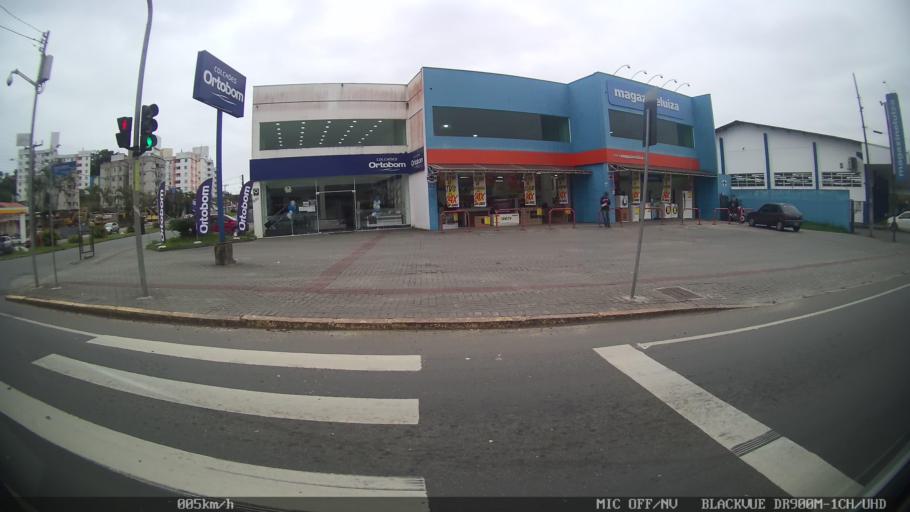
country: BR
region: Santa Catarina
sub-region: Joinville
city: Joinville
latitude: -26.3338
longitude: -48.8474
